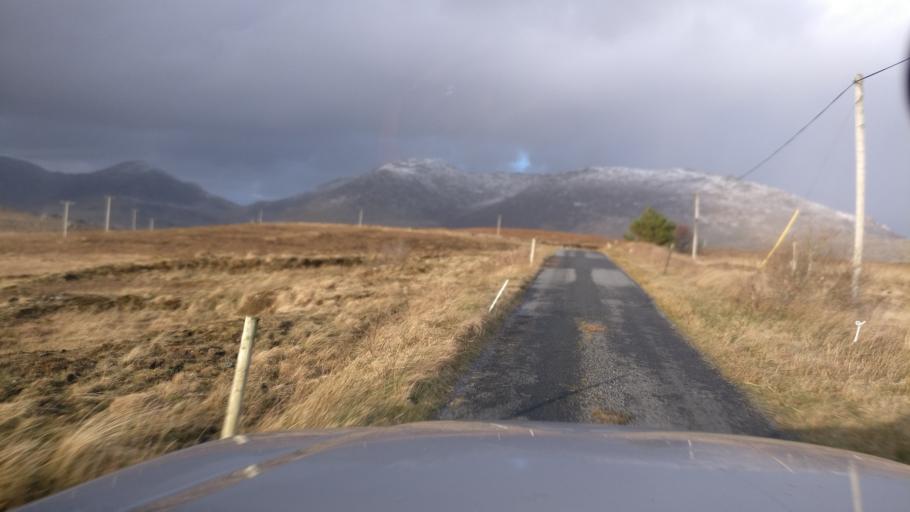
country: IE
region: Connaught
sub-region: County Galway
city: Clifden
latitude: 53.4710
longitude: -9.6924
